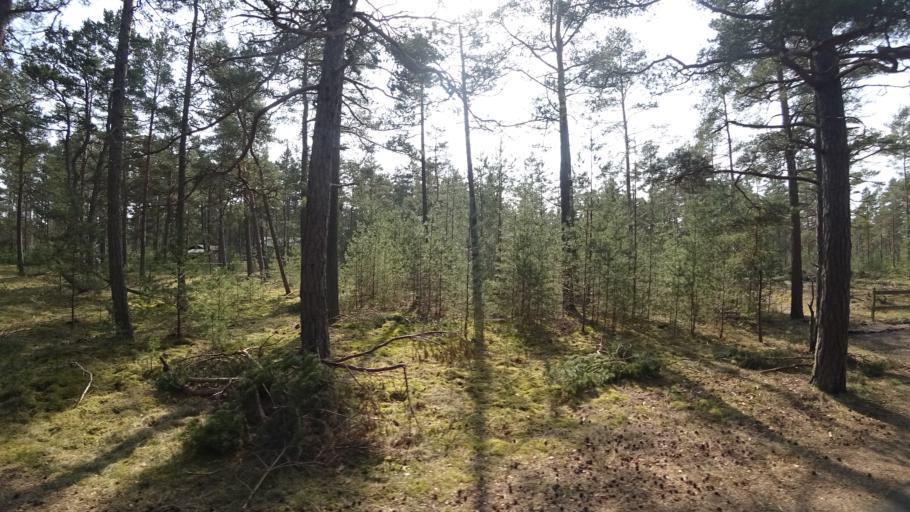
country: SE
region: Skane
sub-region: Kristianstads Kommun
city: Ahus
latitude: 55.9455
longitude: 14.3131
